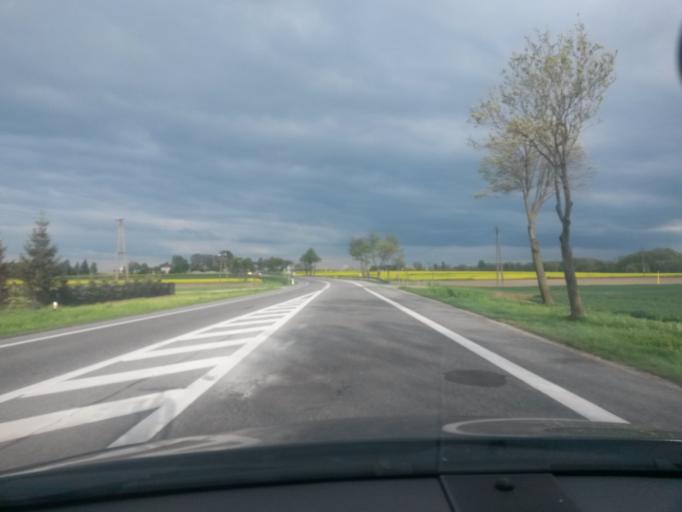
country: PL
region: Masovian Voivodeship
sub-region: Powiat plonski
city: Dzierzaznia
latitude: 52.6300
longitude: 20.1868
